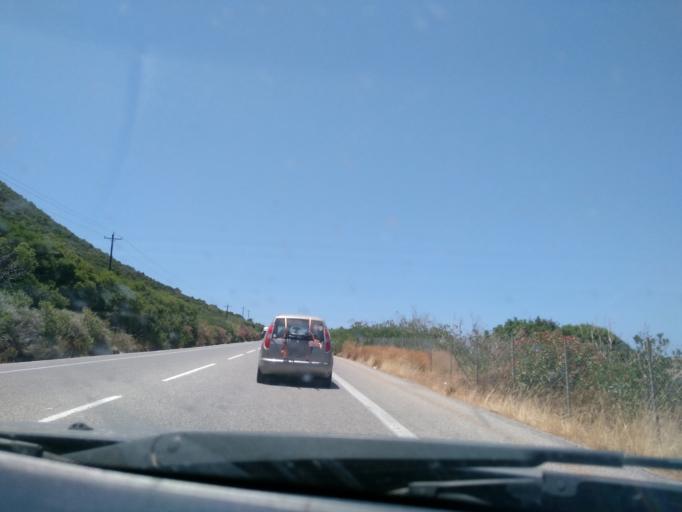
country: GR
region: Crete
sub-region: Nomos Rethymnis
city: Zoniana
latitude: 35.4064
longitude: 24.8315
